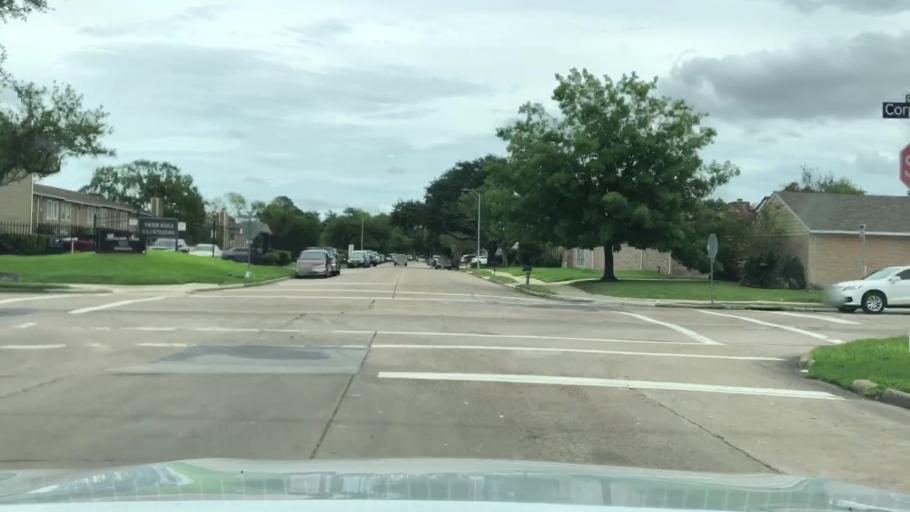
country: US
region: Texas
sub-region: Fort Bend County
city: Meadows Place
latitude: 29.7006
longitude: -95.5527
